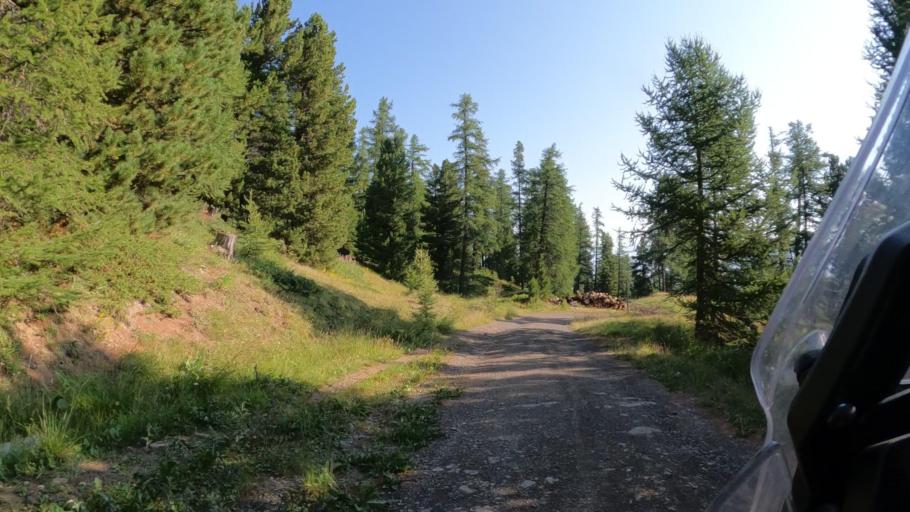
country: FR
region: Provence-Alpes-Cote d'Azur
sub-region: Departement des Hautes-Alpes
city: Guillestre
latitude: 44.6155
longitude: 6.6462
